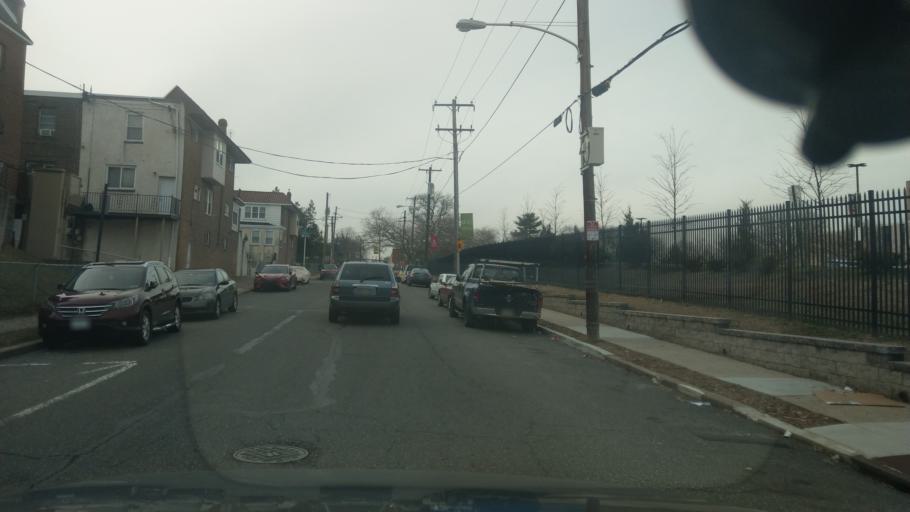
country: US
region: Pennsylvania
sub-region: Montgomery County
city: Wyncote
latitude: 40.0456
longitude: -75.1393
